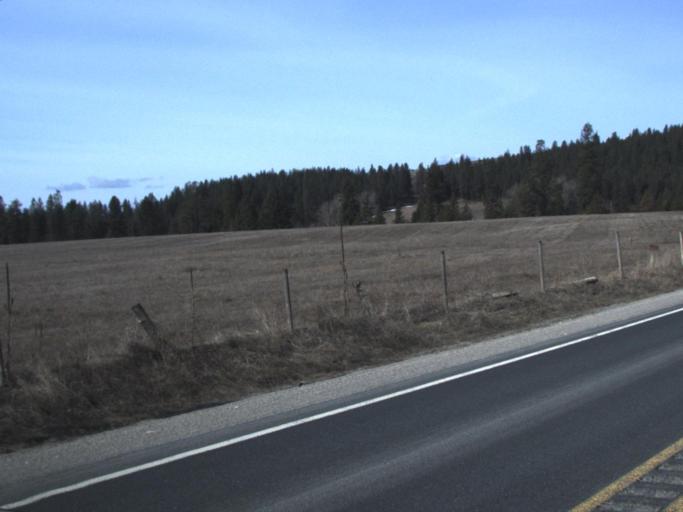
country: US
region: Washington
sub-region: Stevens County
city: Colville
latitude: 48.5102
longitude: -117.7268
